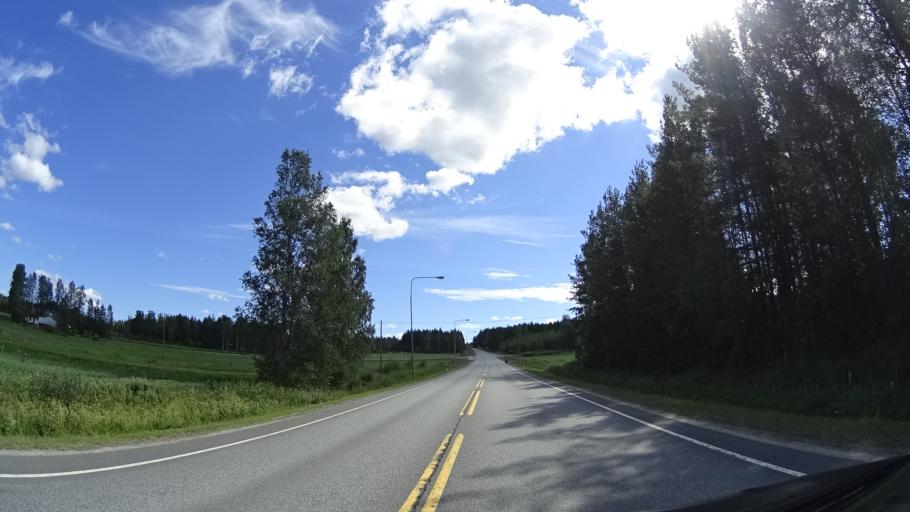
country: FI
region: Pirkanmaa
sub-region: Luoteis-Pirkanmaa
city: Kihnioe
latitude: 62.1989
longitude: 23.1854
